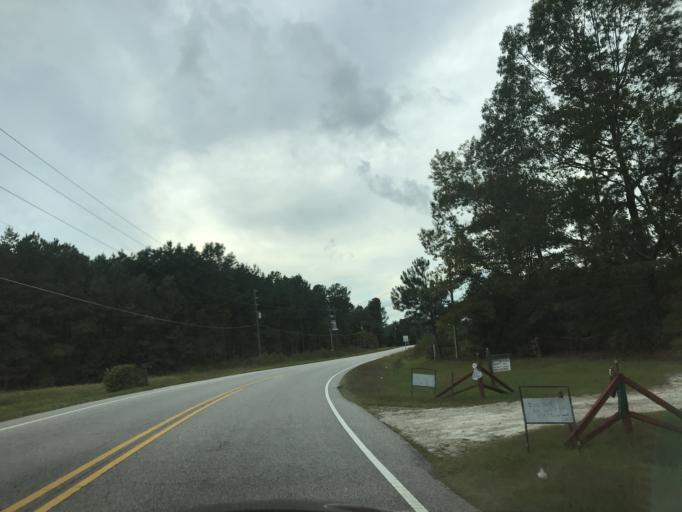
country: US
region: North Carolina
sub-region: Wake County
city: Rolesville
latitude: 35.9831
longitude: -78.3885
